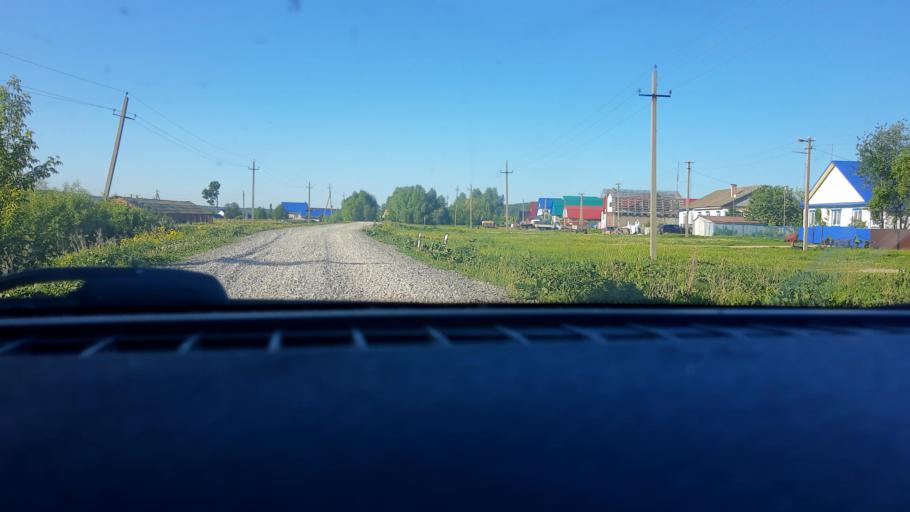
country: RU
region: Bashkortostan
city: Ulukulevo
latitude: 54.5608
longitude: 56.3353
